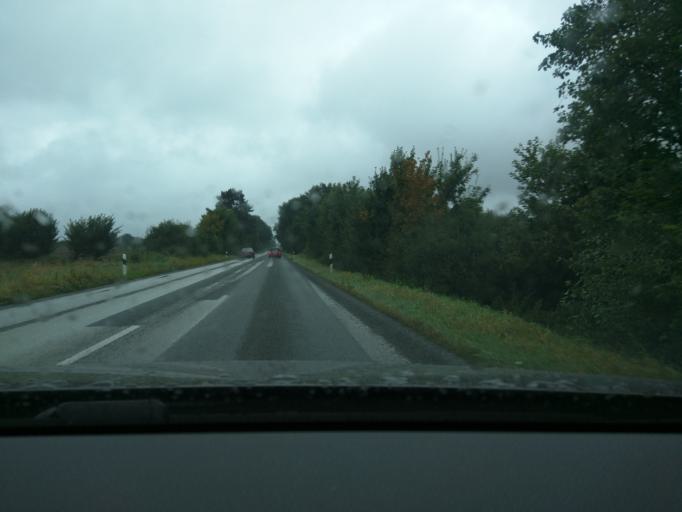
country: DE
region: Schleswig-Holstein
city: Lutau
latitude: 53.4192
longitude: 10.5374
